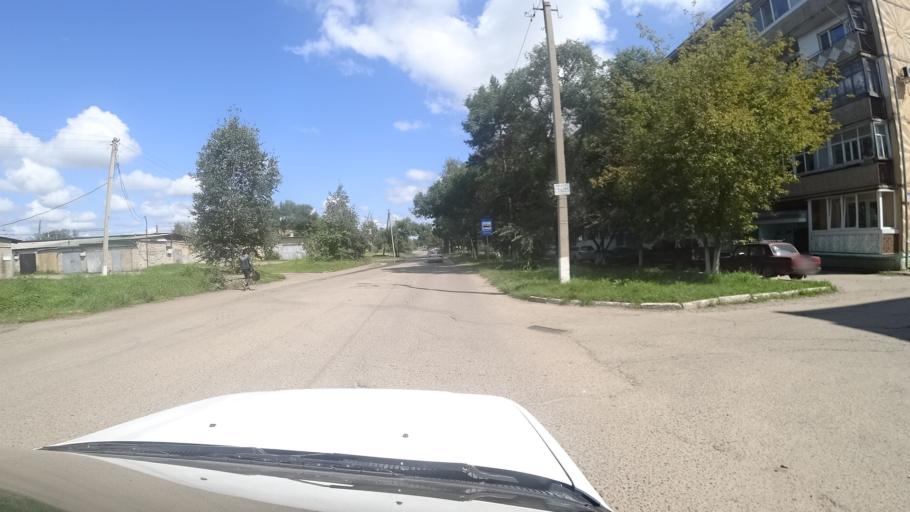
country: RU
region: Primorskiy
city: Dal'nerechensk
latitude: 45.9366
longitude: 133.7307
